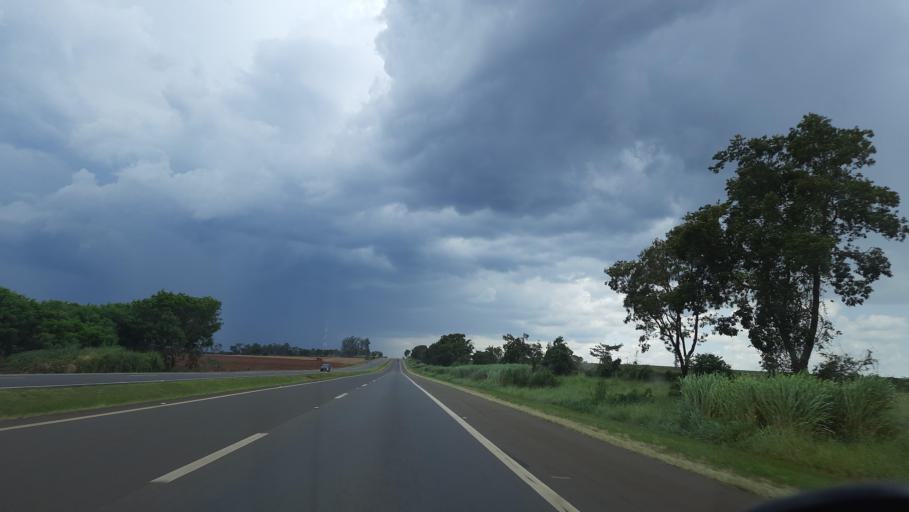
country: BR
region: Sao Paulo
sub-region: Aguai
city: Aguai
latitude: -22.0267
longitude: -47.0336
